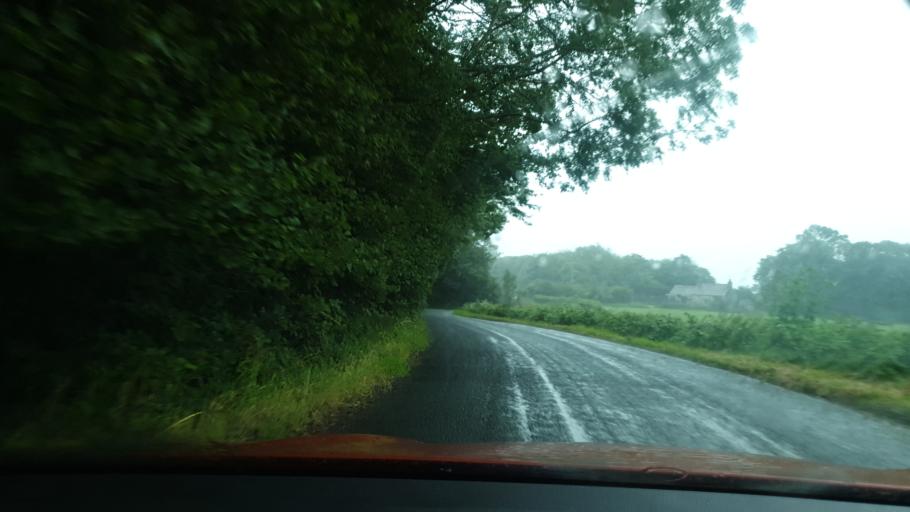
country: GB
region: England
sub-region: Cumbria
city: Millom
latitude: 54.2852
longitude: -3.2322
